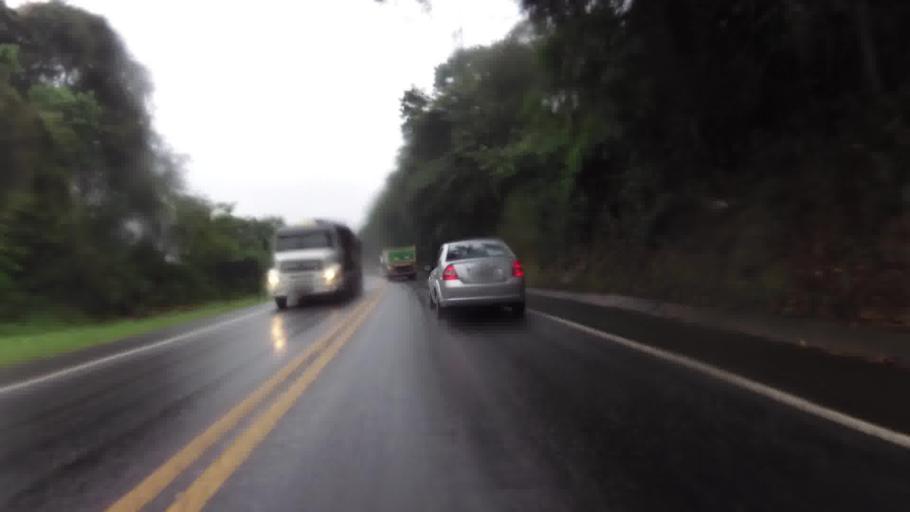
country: BR
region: Espirito Santo
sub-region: Iconha
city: Iconha
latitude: -20.8115
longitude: -40.8387
